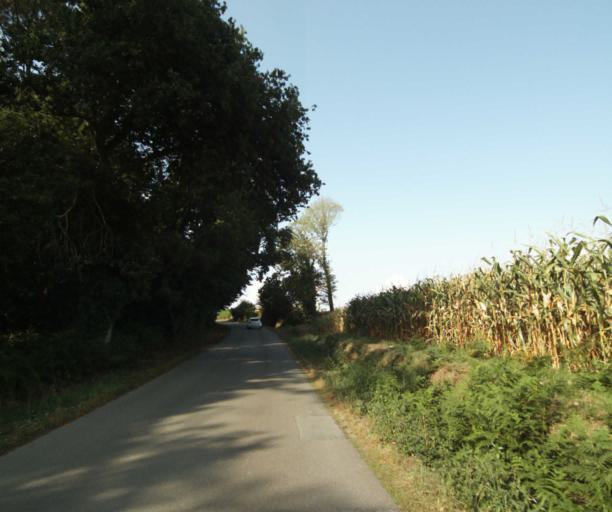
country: FR
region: Brittany
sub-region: Departement du Morbihan
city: Riantec
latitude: 47.7262
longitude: -3.2963
